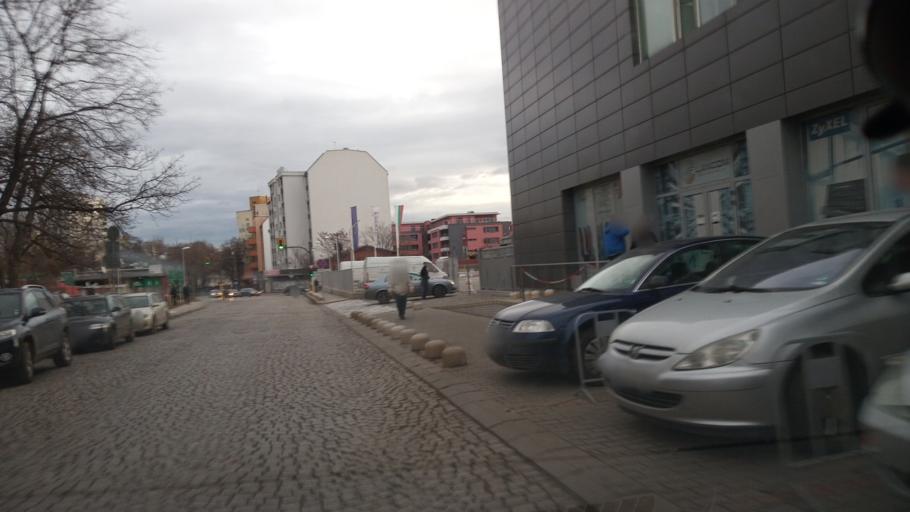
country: BG
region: Sofia-Capital
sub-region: Stolichna Obshtina
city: Sofia
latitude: 42.6913
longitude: 23.2942
